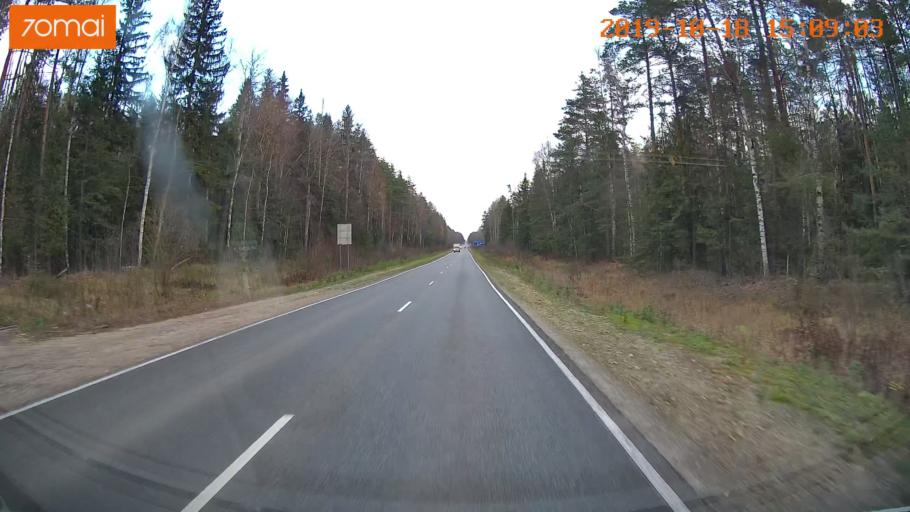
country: RU
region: Vladimir
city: Gus'-Khrustal'nyy
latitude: 55.5608
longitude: 40.6170
